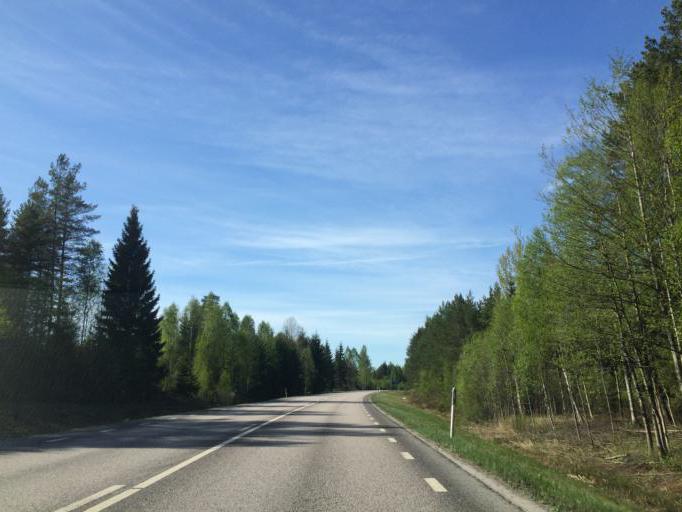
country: SE
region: Soedermanland
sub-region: Katrineholms Kommun
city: Katrineholm
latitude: 59.0770
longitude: 16.2111
